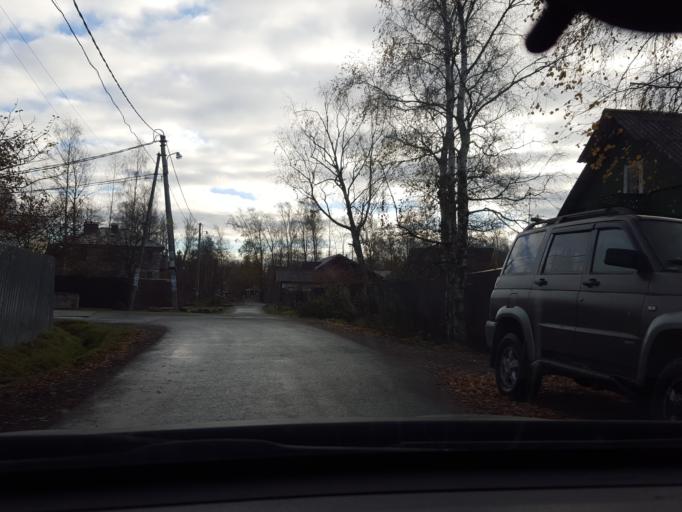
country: RU
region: St.-Petersburg
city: Shuvalovo
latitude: 60.0397
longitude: 30.2939
